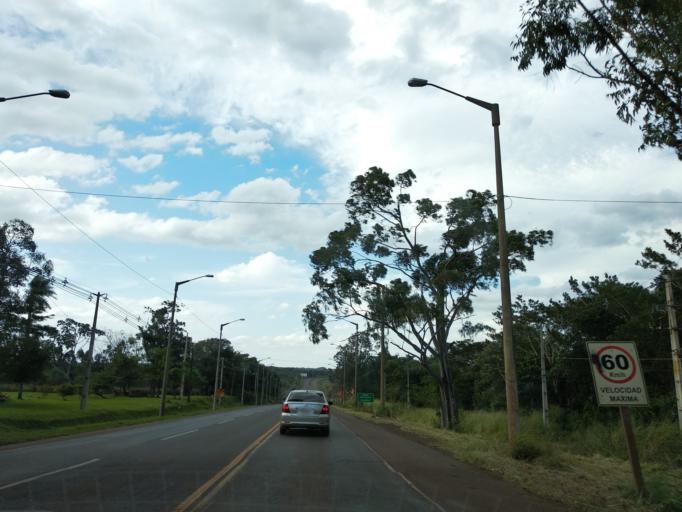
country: PY
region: Itapua
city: San Juan del Parana
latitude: -27.2925
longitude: -55.9234
